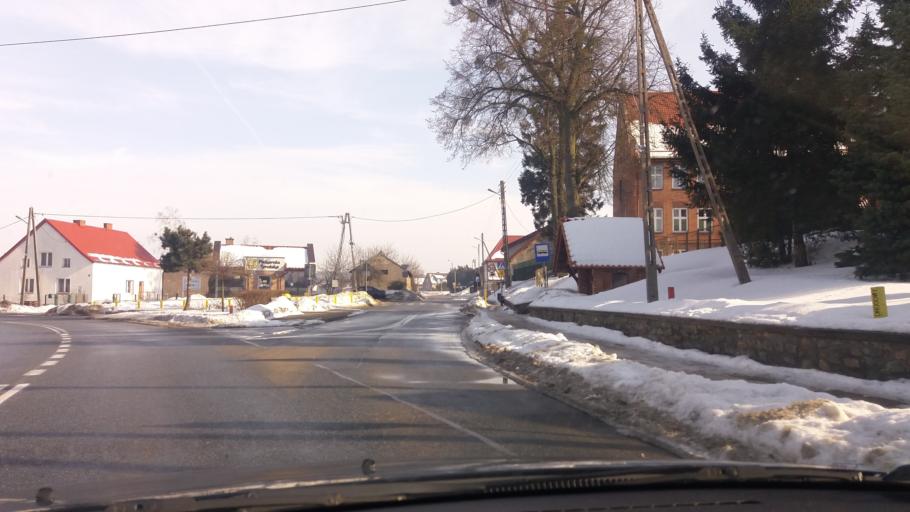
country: PL
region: Warmian-Masurian Voivodeship
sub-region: Powiat szczycienski
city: Dzwierzuty
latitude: 53.7035
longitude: 20.9594
